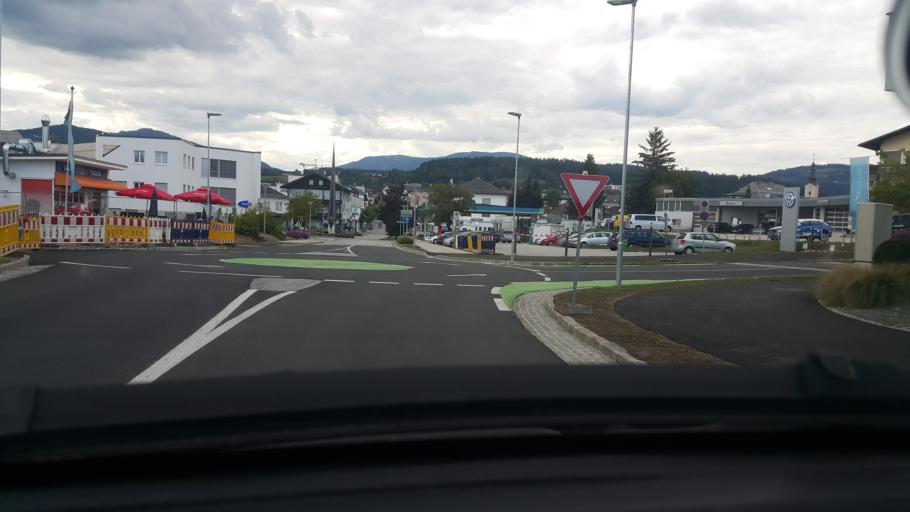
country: AT
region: Carinthia
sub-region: Politischer Bezirk Feldkirchen
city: Feldkirchen in Karnten
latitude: 46.7222
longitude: 14.0978
